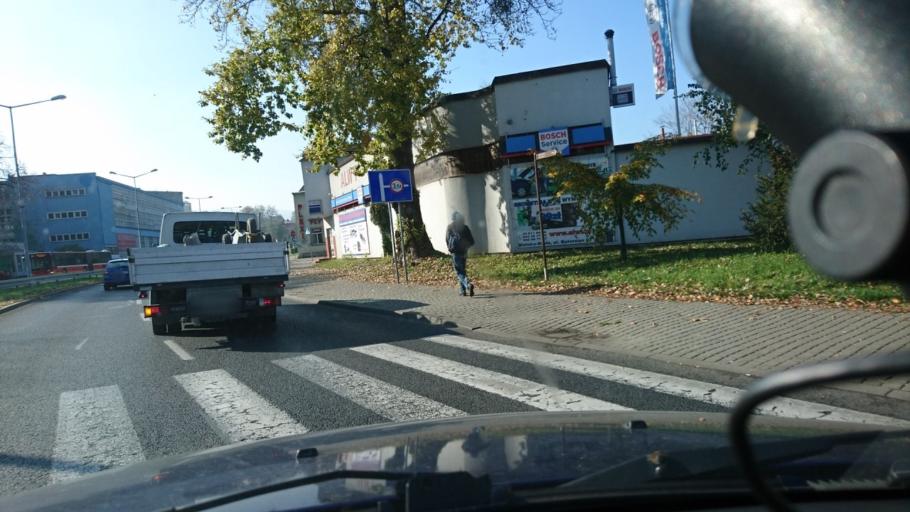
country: PL
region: Silesian Voivodeship
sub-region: Bielsko-Biala
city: Bielsko-Biala
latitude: 49.8103
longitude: 19.0452
